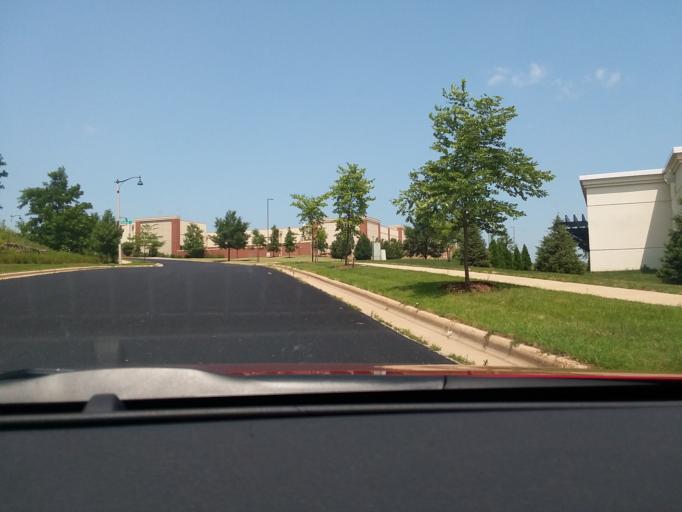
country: US
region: Wisconsin
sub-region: Dane County
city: Fitchburg
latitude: 43.0119
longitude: -89.4785
